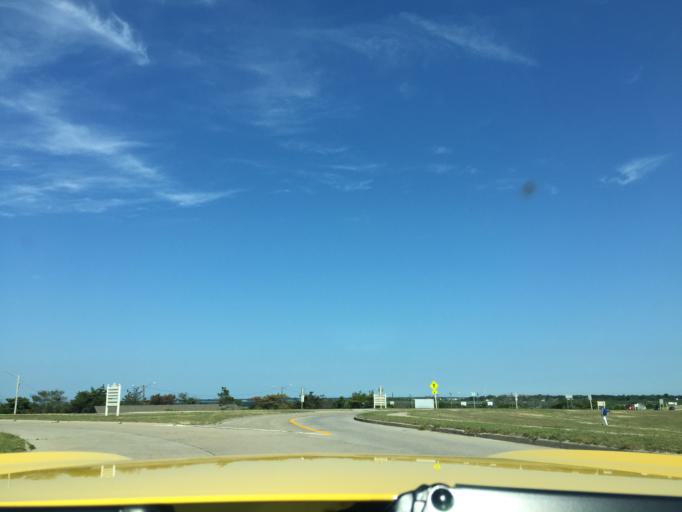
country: US
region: New York
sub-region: Suffolk County
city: Mastic Beach
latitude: 40.7337
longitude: -72.8653
